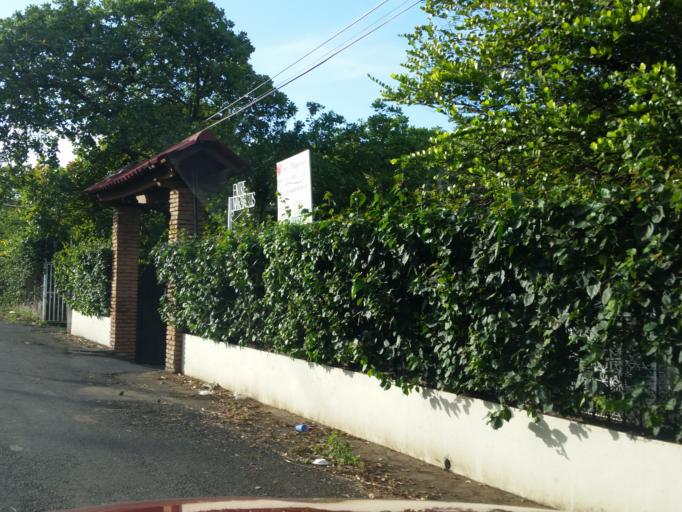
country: NI
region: Managua
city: Managua
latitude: 12.0864
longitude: -86.2306
